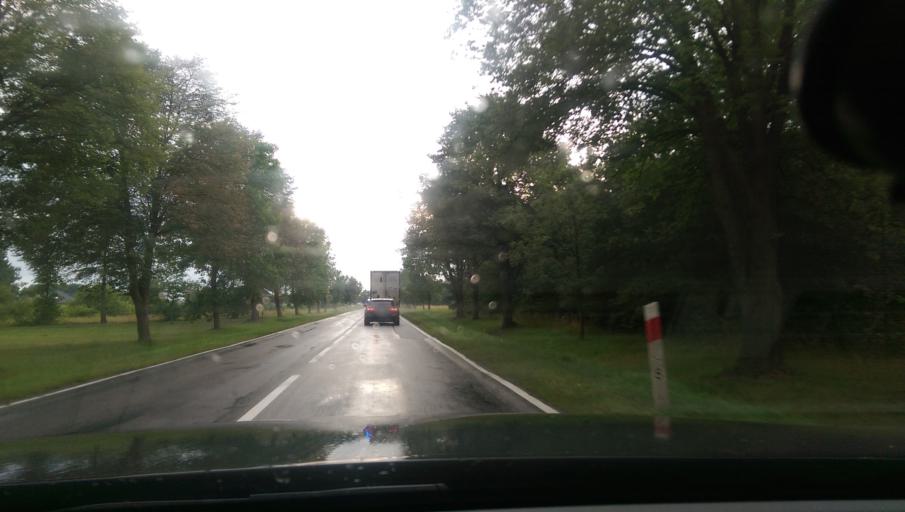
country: PL
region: Warmian-Masurian Voivodeship
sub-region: Powiat szczycienski
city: Swietajno
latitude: 53.5569
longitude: 21.1279
